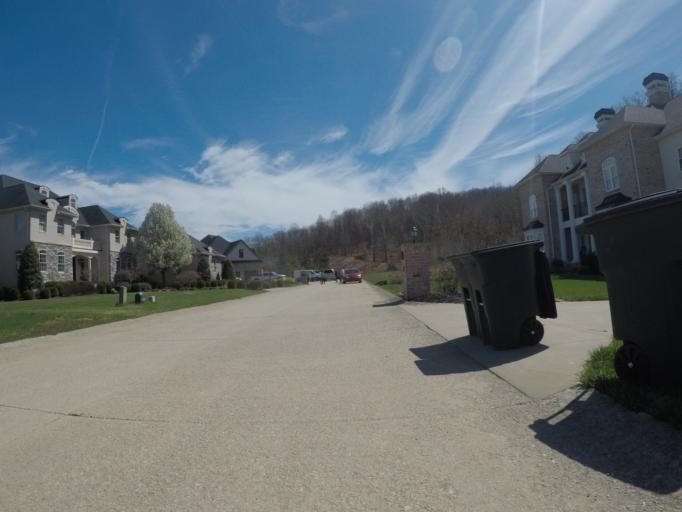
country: US
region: West Virginia
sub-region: Cabell County
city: Pea Ridge
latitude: 38.4069
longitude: -82.3085
